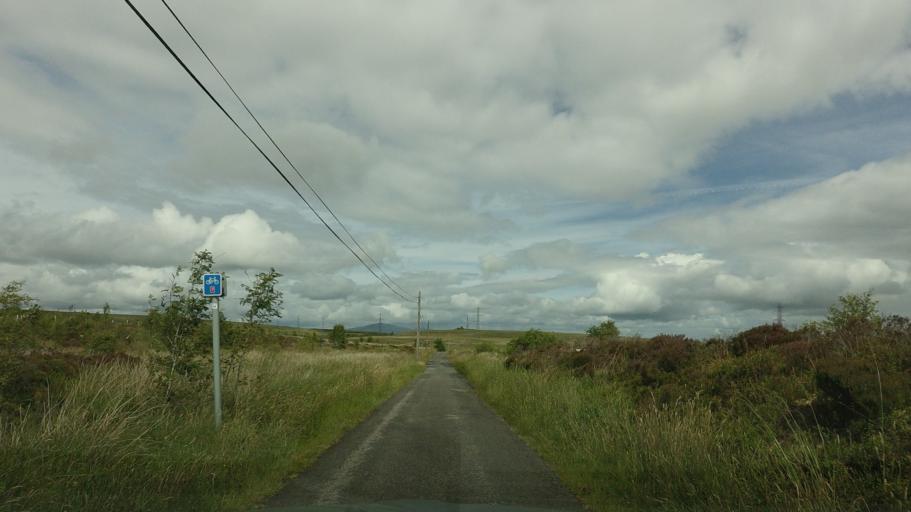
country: GB
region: Scotland
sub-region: Stirling
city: Killearn
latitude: 56.0893
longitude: -4.4342
